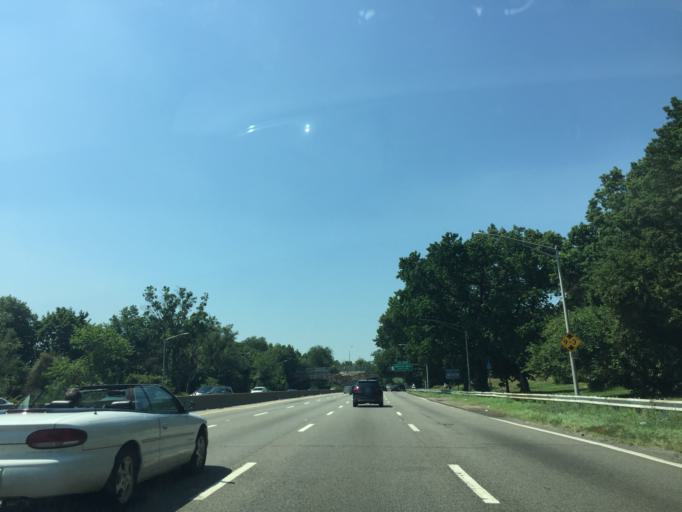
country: US
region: New York
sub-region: Nassau County
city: Valley Stream
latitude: 40.6804
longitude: -73.7288
